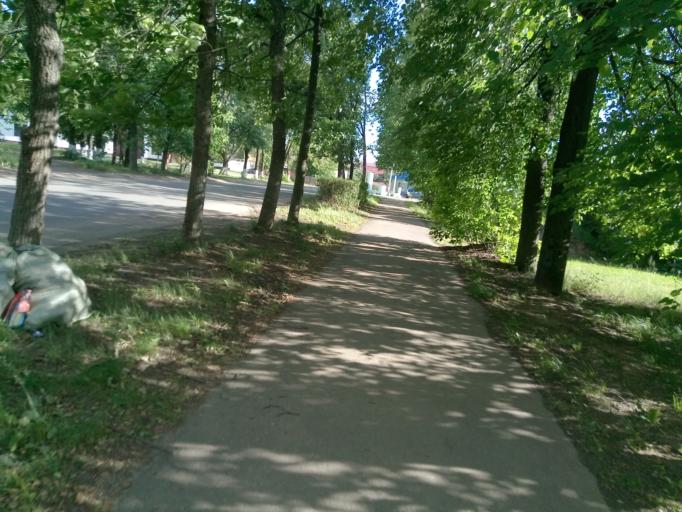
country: RU
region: Jaroslavl
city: Yaroslavl
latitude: 57.6391
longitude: 39.9119
